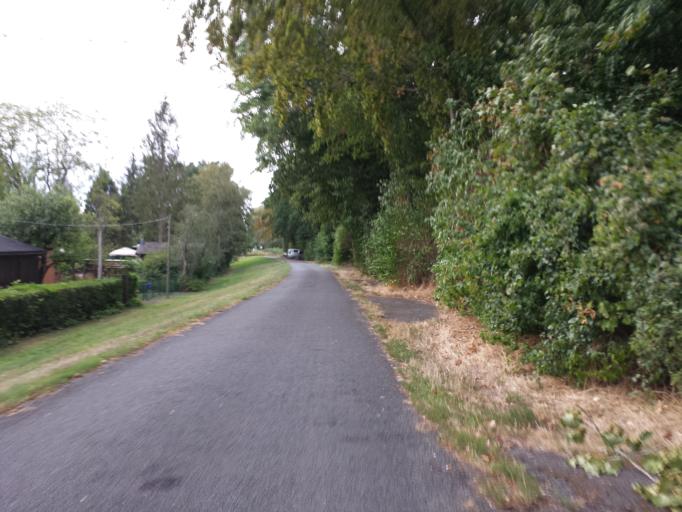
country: DE
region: Lower Saxony
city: Stuhr
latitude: 53.0659
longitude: 8.7675
